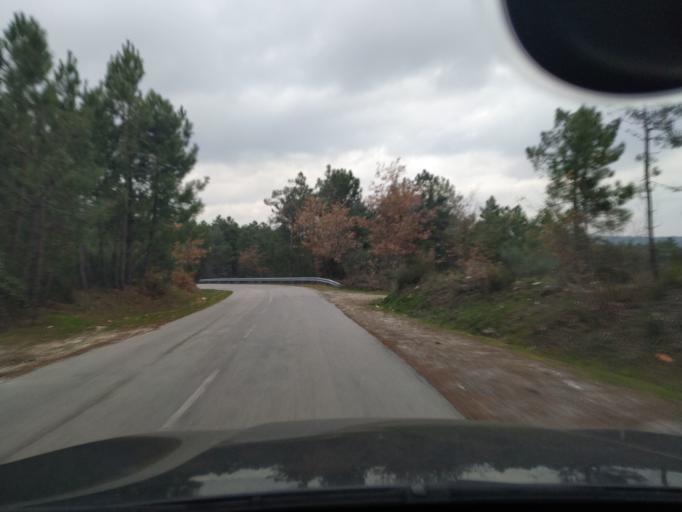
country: PT
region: Vila Real
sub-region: Sabrosa
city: Sabrosa
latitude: 41.3350
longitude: -7.6486
